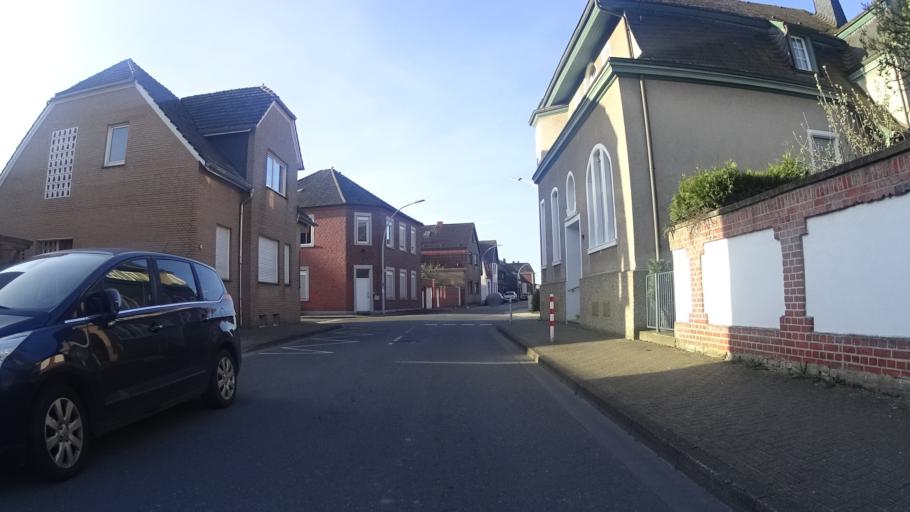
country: DE
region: North Rhine-Westphalia
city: Emsdetten
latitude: 52.1771
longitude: 7.5235
